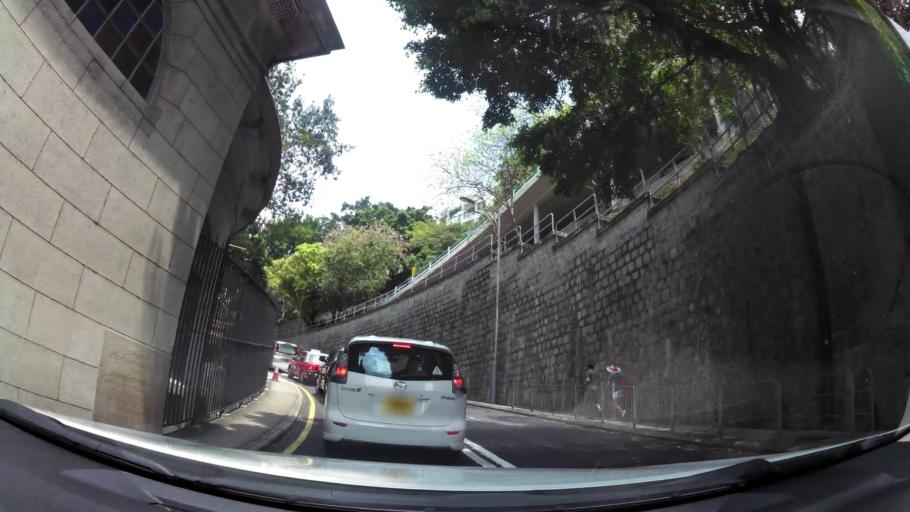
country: HK
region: Wanchai
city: Wan Chai
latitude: 22.2741
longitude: 114.1846
